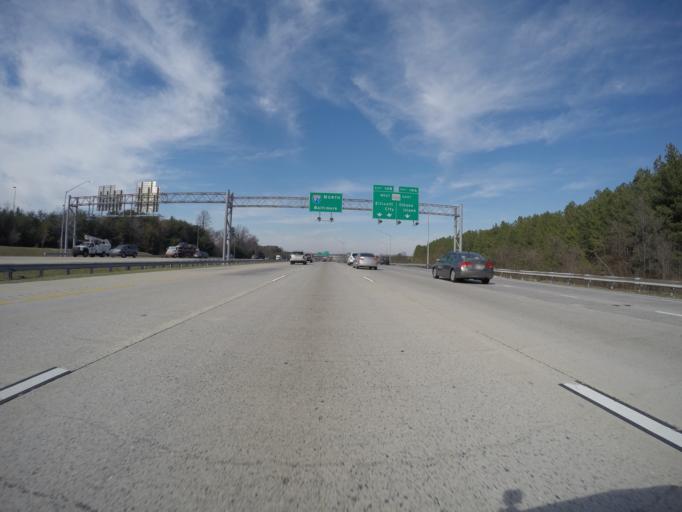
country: US
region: Maryland
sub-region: Anne Arundel County
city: South Gate
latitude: 39.1456
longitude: -76.6445
